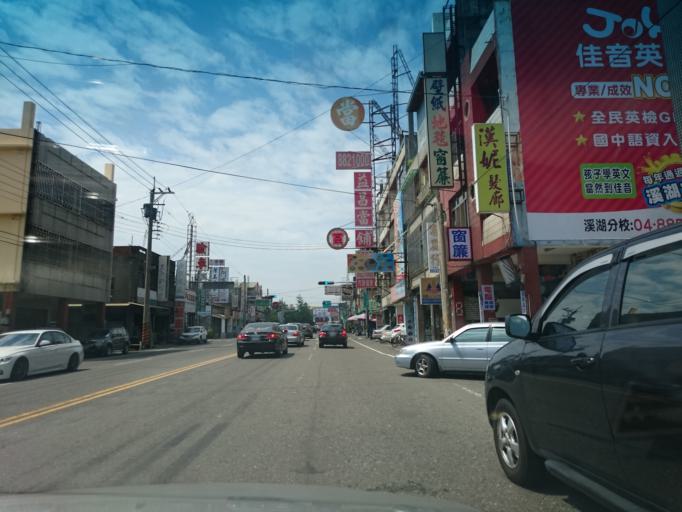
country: TW
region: Taiwan
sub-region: Changhua
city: Chang-hua
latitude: 23.9568
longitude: 120.4854
